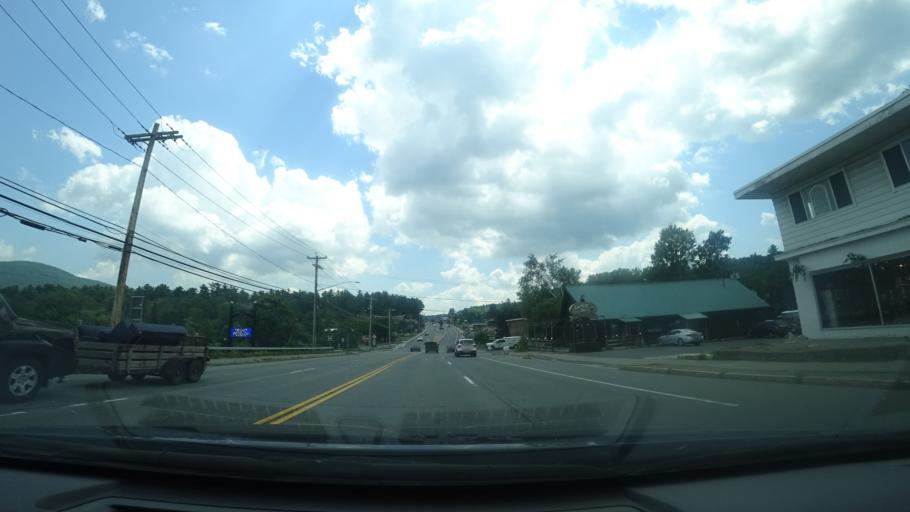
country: US
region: New York
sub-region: Warren County
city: Glens Falls North
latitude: 43.4184
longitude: -73.7136
